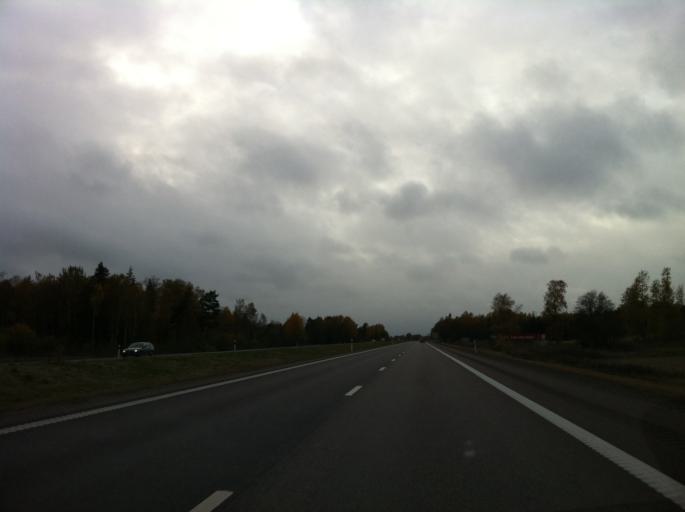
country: SE
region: OEstergoetland
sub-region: Odeshogs Kommun
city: OEdeshoeg
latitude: 58.2415
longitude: 14.7360
